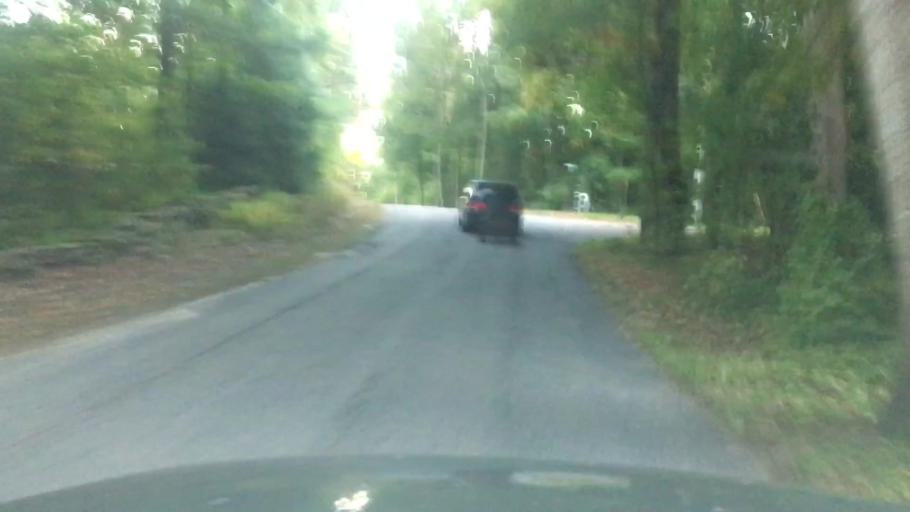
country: US
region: Massachusetts
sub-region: Worcester County
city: Southbridge
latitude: 42.1222
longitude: -72.0297
